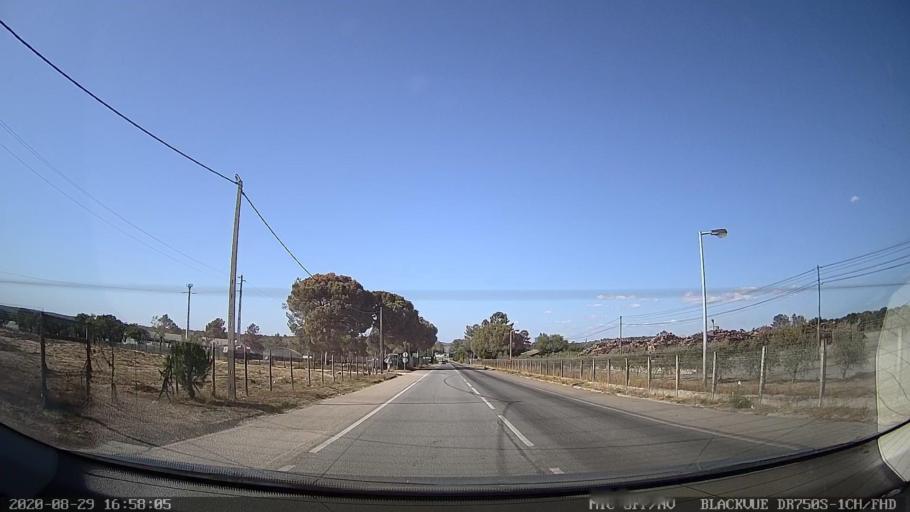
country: PT
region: Setubal
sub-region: Alcacer do Sal
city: Alcacer do Sal
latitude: 38.3984
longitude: -8.5146
